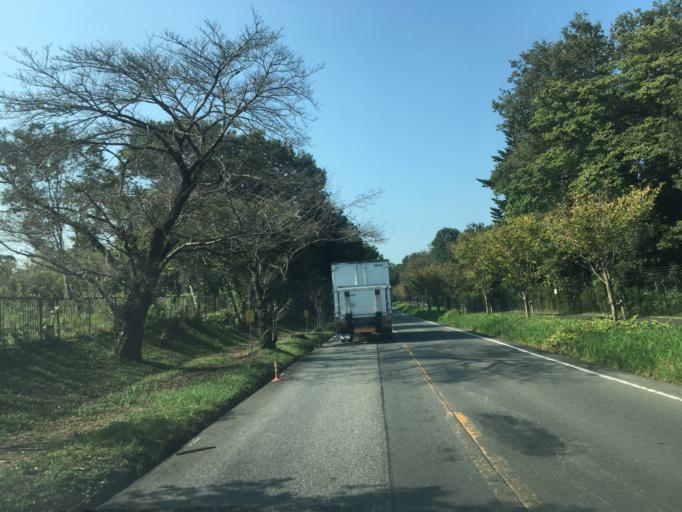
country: JP
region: Tokyo
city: Higashimurayama-shi
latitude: 35.7704
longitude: 139.4146
